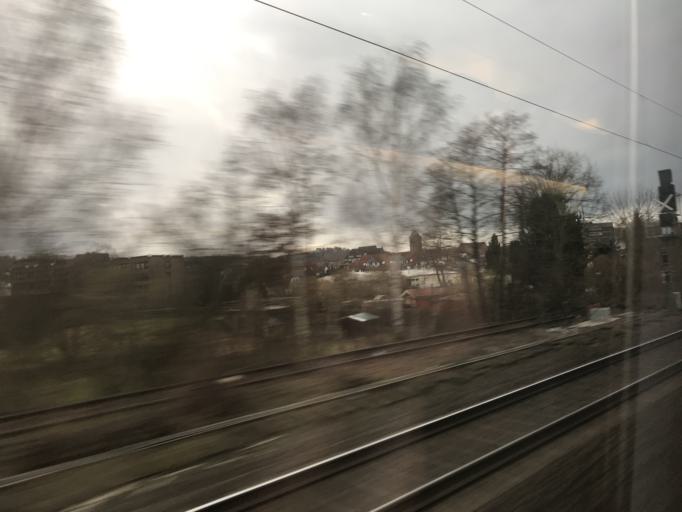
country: DE
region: Hesse
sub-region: Regierungsbezirk Kassel
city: Bad Hersfeld
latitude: 50.8632
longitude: 9.7142
